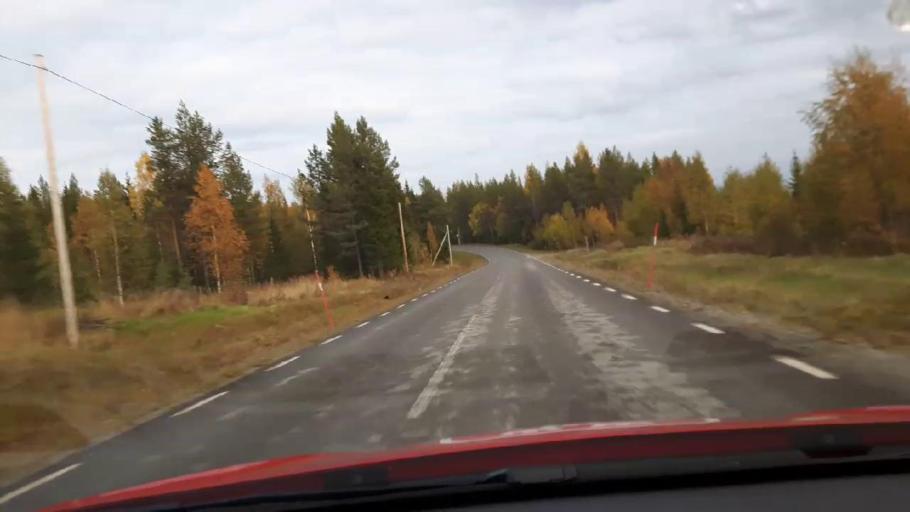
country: SE
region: Jaemtland
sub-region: OEstersunds Kommun
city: Lit
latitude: 63.3105
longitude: 15.1236
